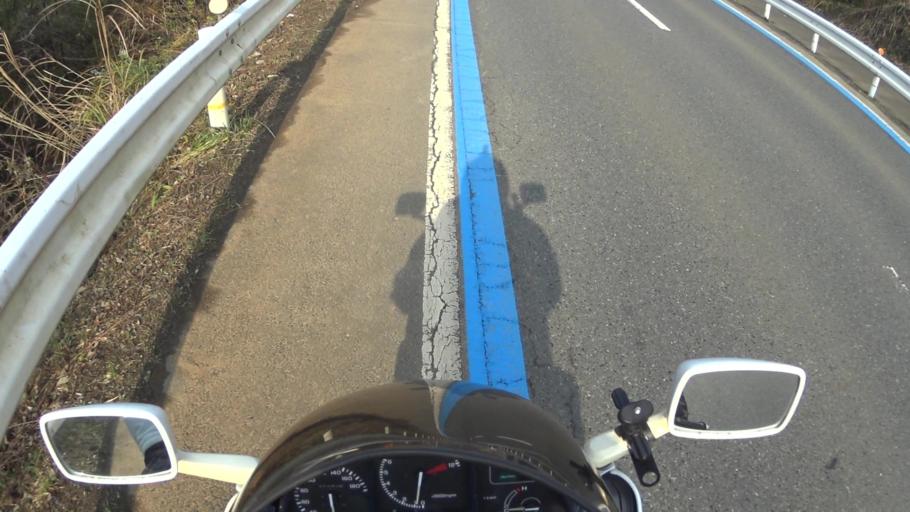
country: JP
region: Kyoto
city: Fukuchiyama
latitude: 35.3332
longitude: 135.1154
